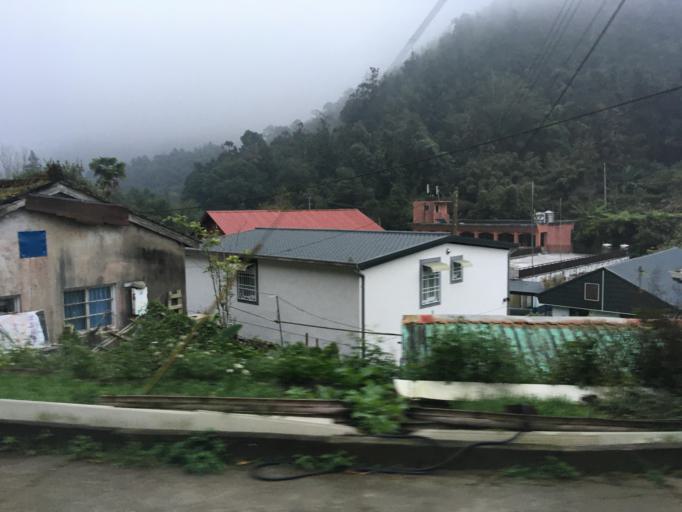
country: TW
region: Taiwan
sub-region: Chiayi
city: Jiayi Shi
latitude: 23.5041
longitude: 120.6595
